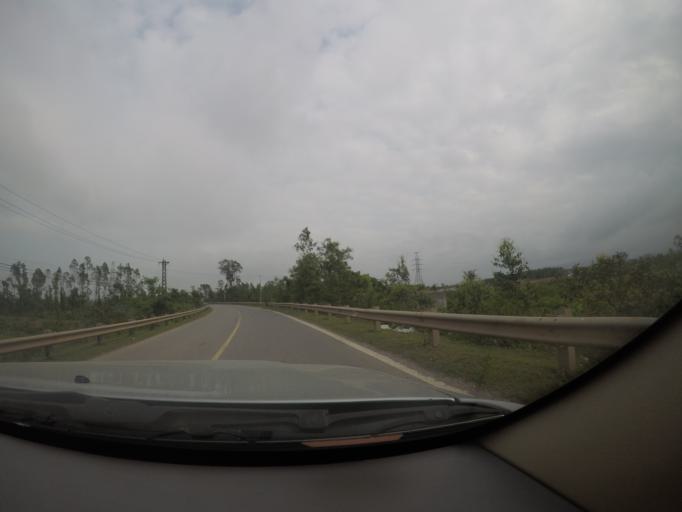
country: VN
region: Quang Binh
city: Kwang Binh
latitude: 17.4296
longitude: 106.5845
